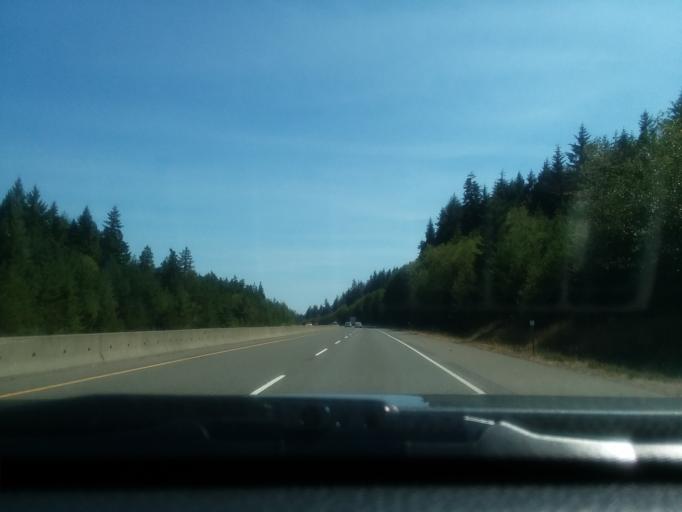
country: CA
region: British Columbia
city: Port Alberni
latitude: 49.4072
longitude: -124.6841
